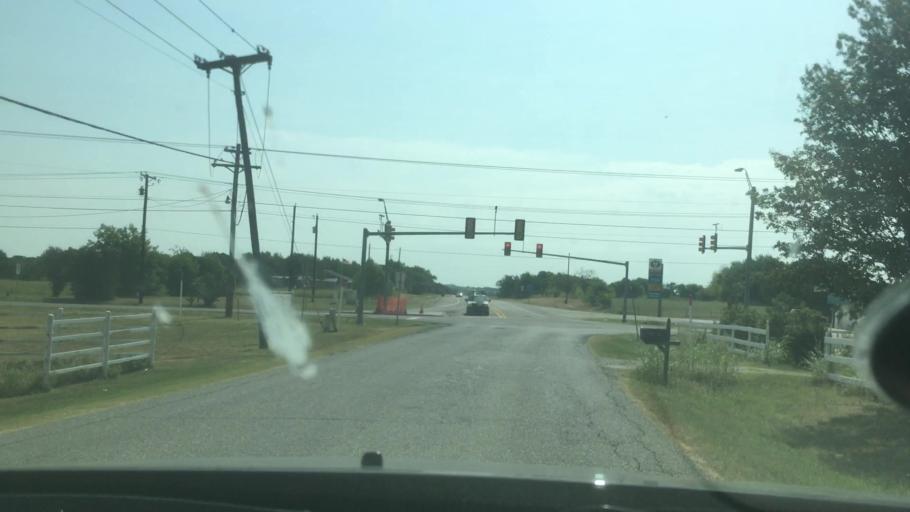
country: US
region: Texas
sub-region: Grayson County
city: Pottsboro
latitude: 33.8020
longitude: -96.6786
